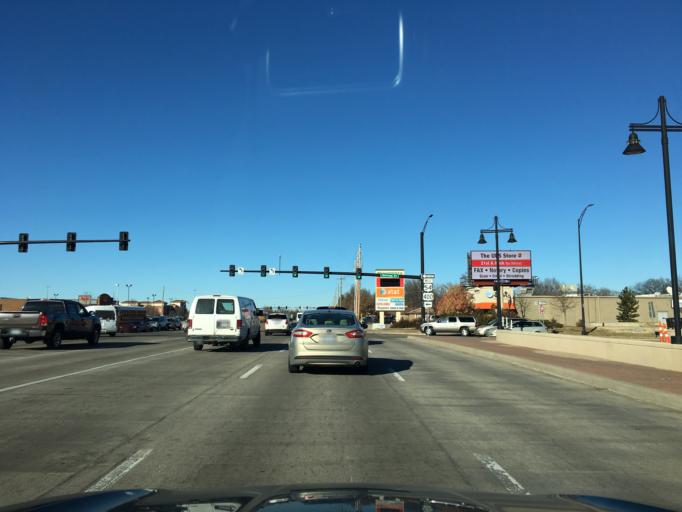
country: US
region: Kansas
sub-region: Sedgwick County
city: Bellaire
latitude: 37.6792
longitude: -97.2443
